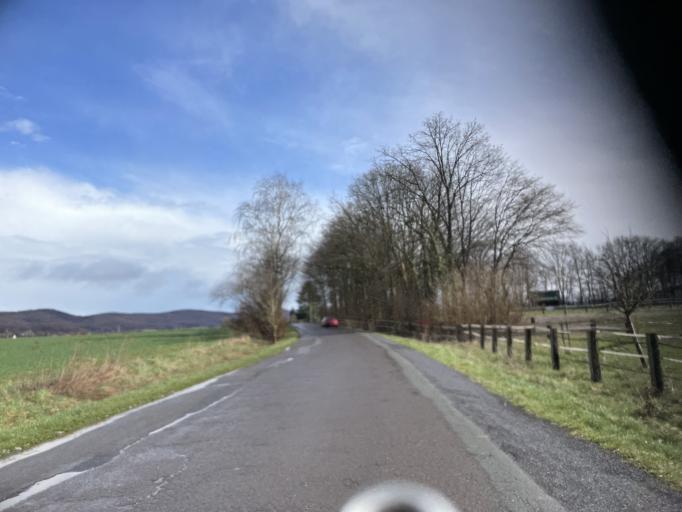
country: DE
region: North Rhine-Westphalia
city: Porta Westfalica
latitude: 52.2261
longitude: 8.9475
